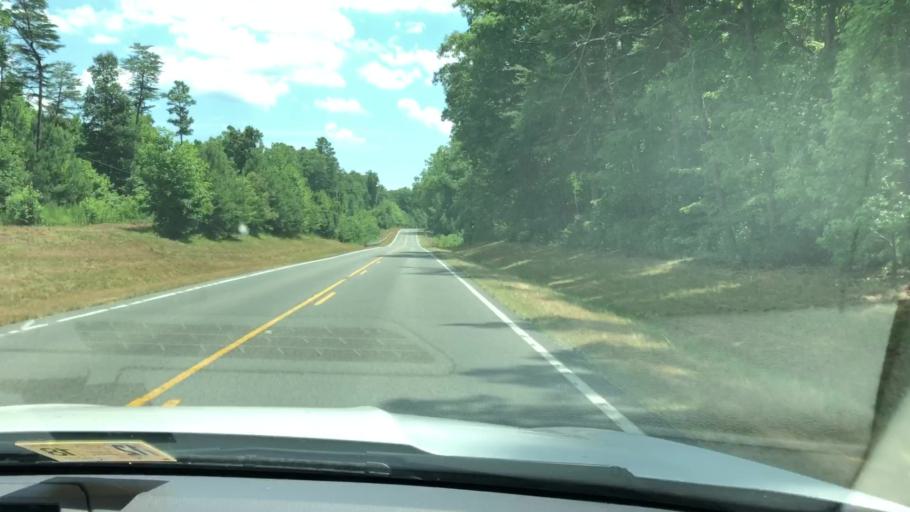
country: US
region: Virginia
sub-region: Lancaster County
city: Lancaster
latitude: 37.8216
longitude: -76.5554
